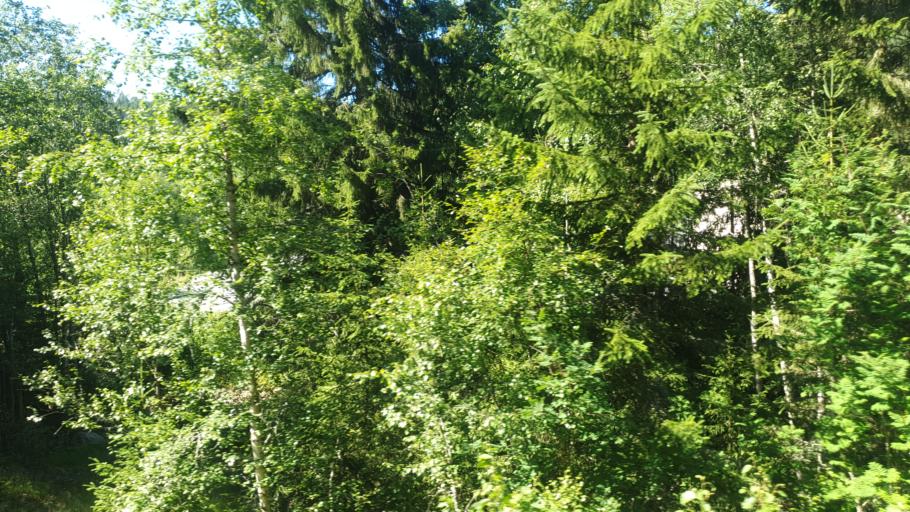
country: NO
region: Sor-Trondelag
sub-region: Meldal
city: Meldal
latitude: 63.1400
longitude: 9.7120
